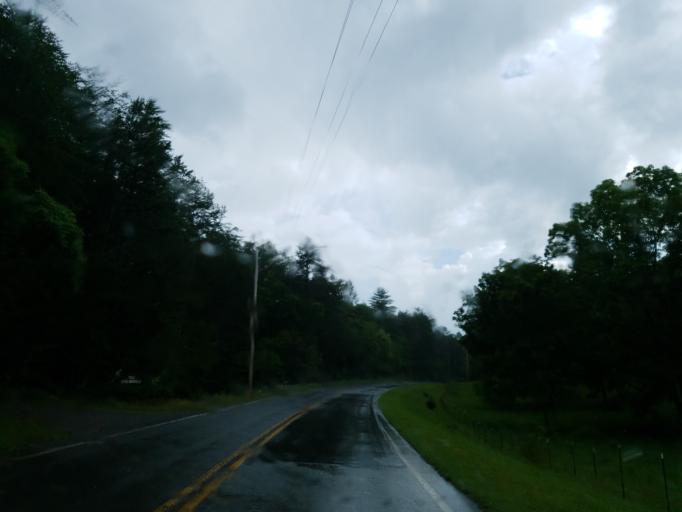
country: US
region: Georgia
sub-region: Fannin County
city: Blue Ridge
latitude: 34.7786
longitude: -84.2488
